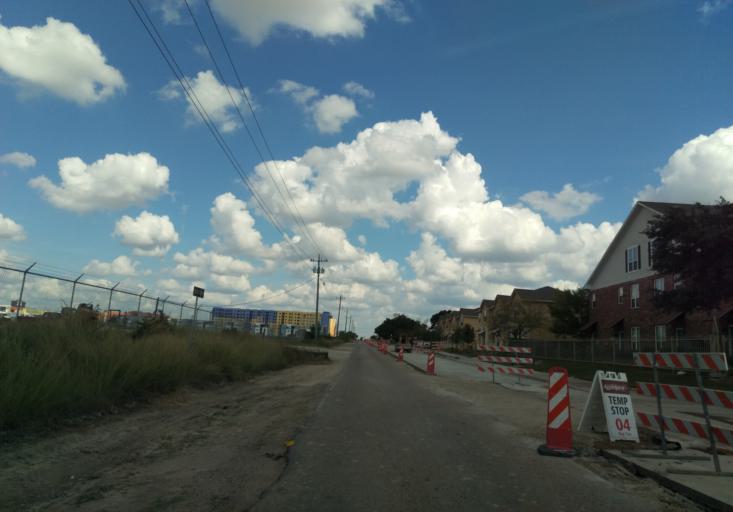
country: US
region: Texas
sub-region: Brazos County
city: College Station
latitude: 30.5921
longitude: -96.3442
